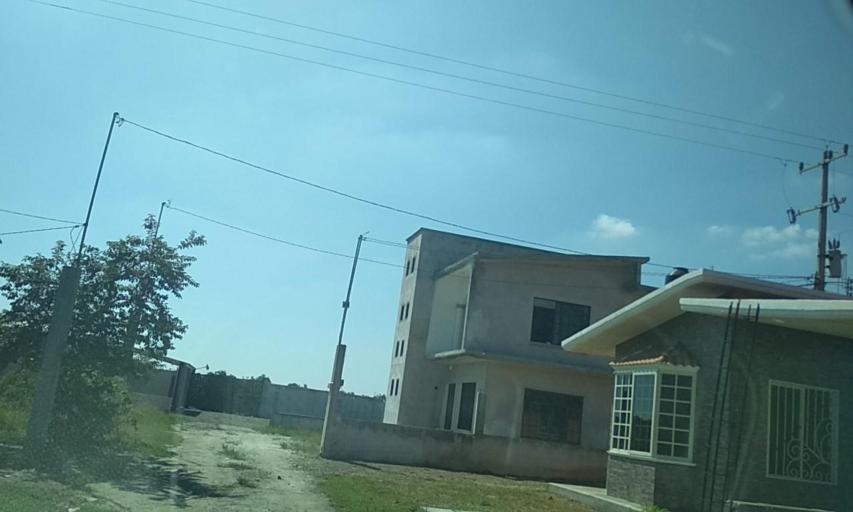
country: MX
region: Veracruz
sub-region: Martinez de la Torre
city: La Union Paso Largo
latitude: 20.1483
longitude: -97.0007
